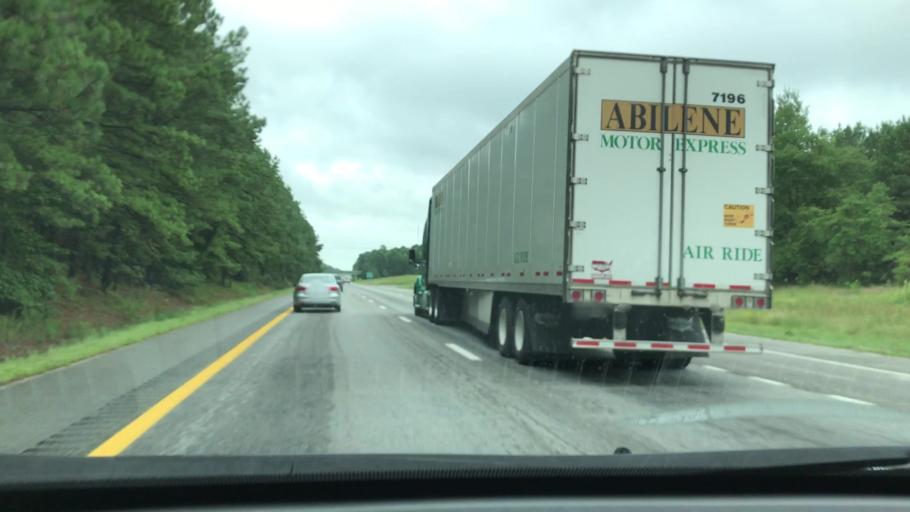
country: US
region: Virginia
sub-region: City of Emporia
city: Emporia
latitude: 36.7991
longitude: -77.4600
